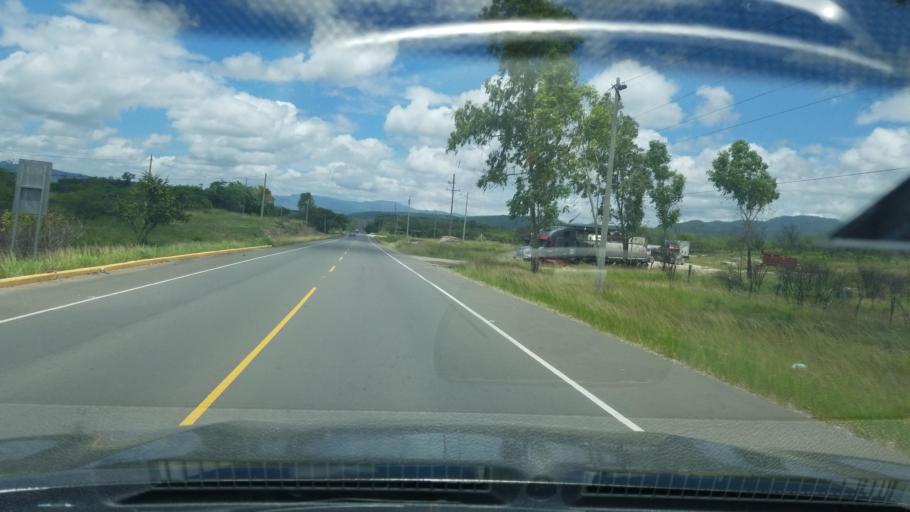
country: HN
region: Francisco Morazan
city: Cofradia
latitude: 14.3029
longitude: -87.2310
